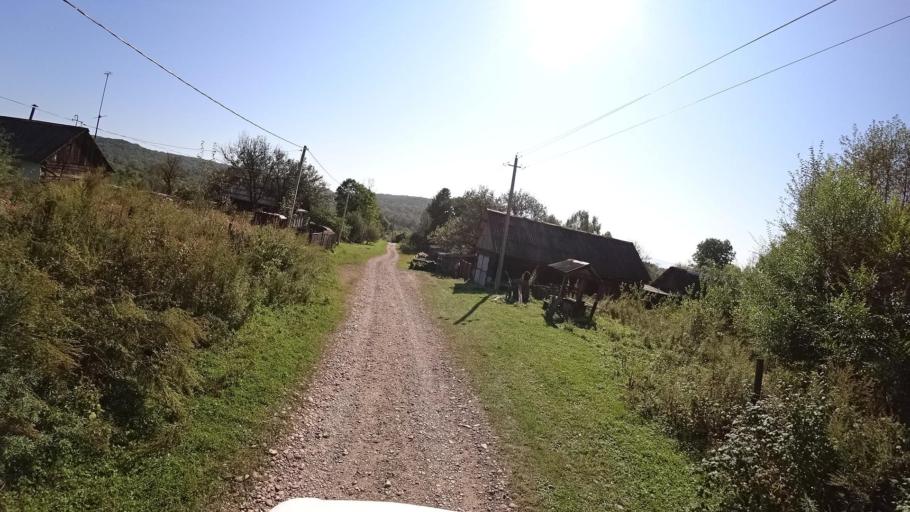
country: RU
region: Jewish Autonomous Oblast
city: Bira
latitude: 49.0024
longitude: 132.4730
